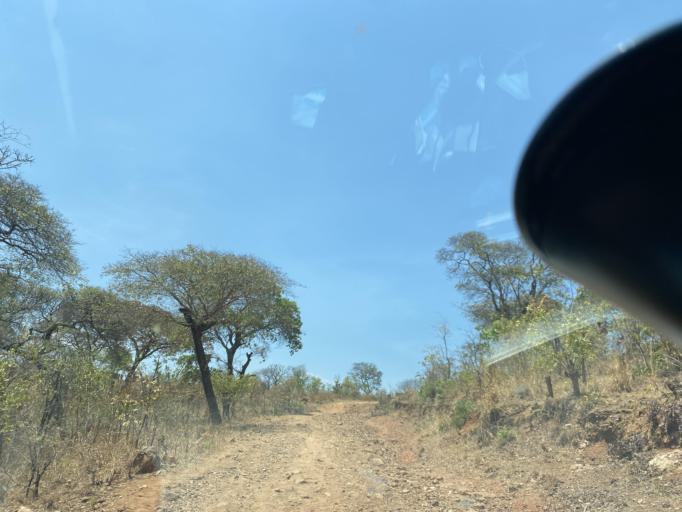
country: ZM
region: Lusaka
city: Kafue
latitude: -15.8054
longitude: 28.4409
